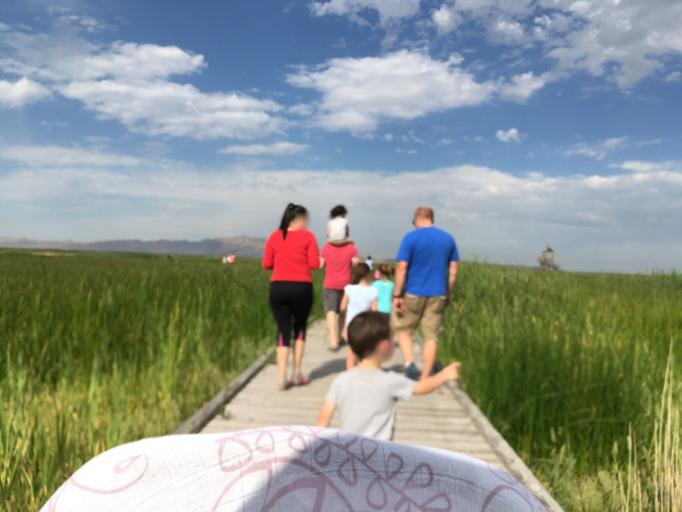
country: US
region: Utah
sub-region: Davis County
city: Layton
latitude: 41.0364
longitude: -112.0254
